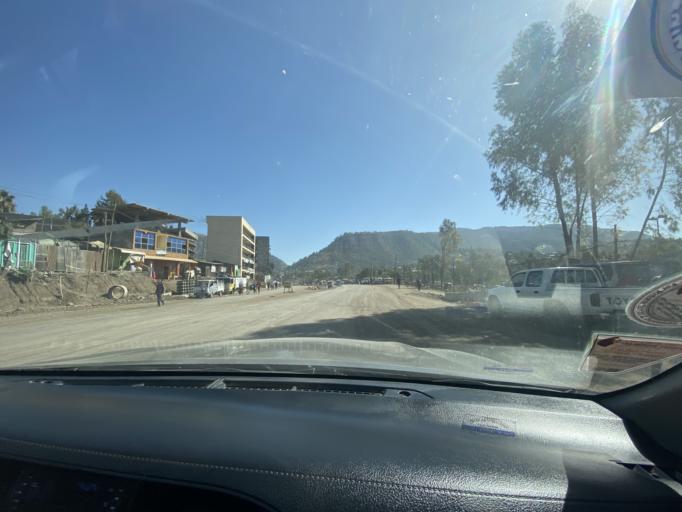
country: ET
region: Amhara
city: Robit
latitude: 11.8267
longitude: 39.5944
